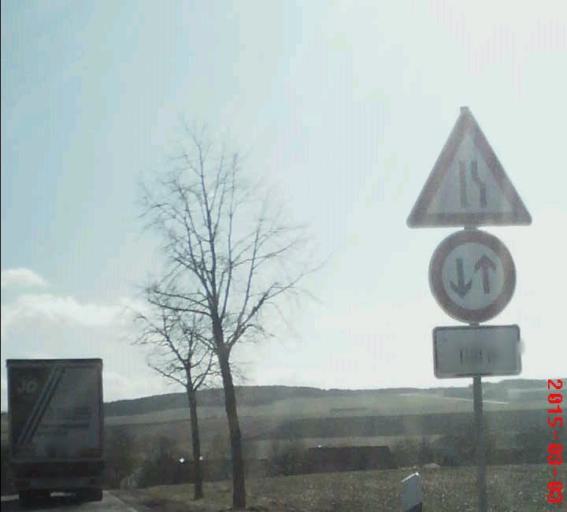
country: DE
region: Thuringia
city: Stadtilm
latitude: 50.7566
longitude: 11.1455
